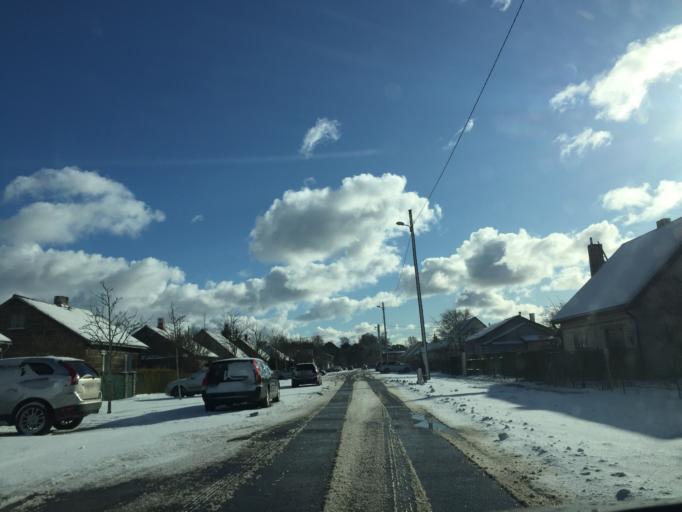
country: LV
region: Ventspils
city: Ventspils
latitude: 57.3815
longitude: 21.5555
